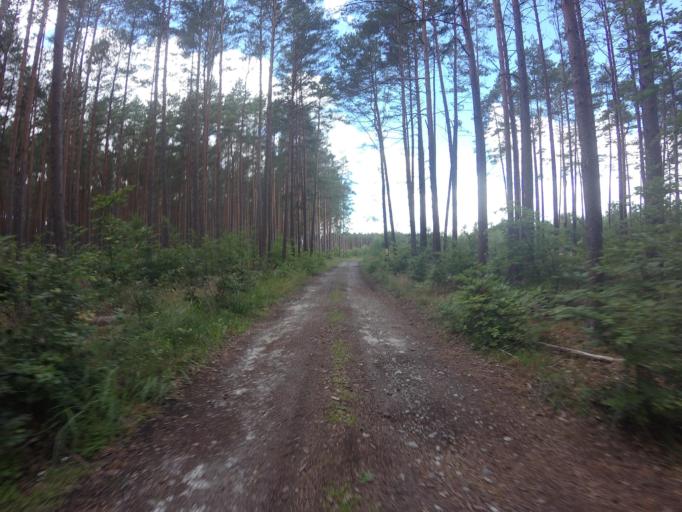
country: PL
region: West Pomeranian Voivodeship
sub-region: Powiat drawski
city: Kalisz Pomorski
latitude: 53.2081
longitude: 15.9137
